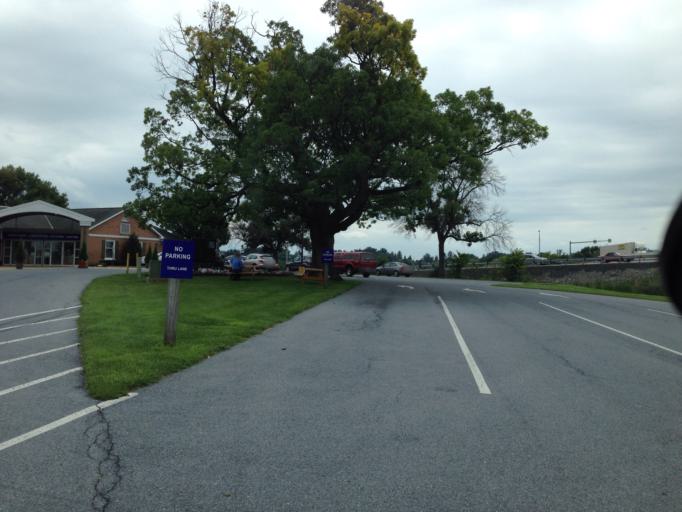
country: US
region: Pennsylvania
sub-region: Lancaster County
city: Lancaster
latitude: 40.0511
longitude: -76.2551
